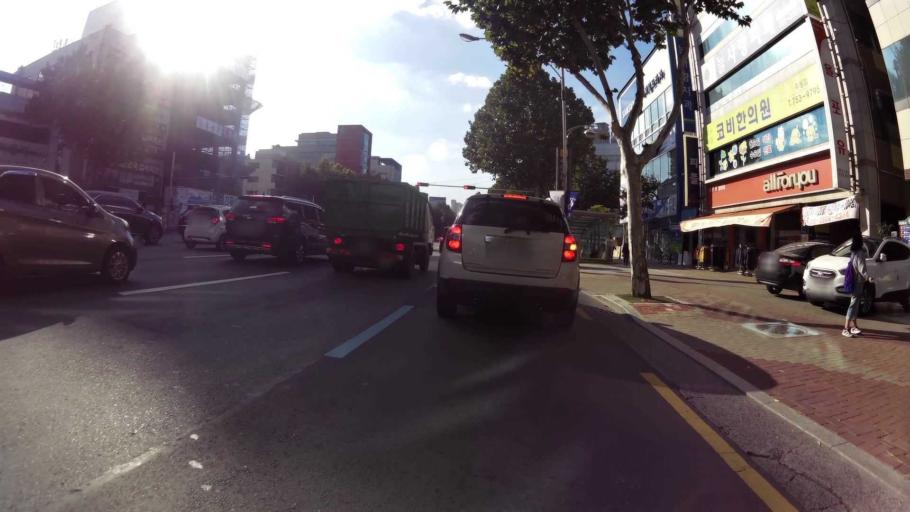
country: KR
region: Daegu
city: Daegu
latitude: 35.8590
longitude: 128.6365
